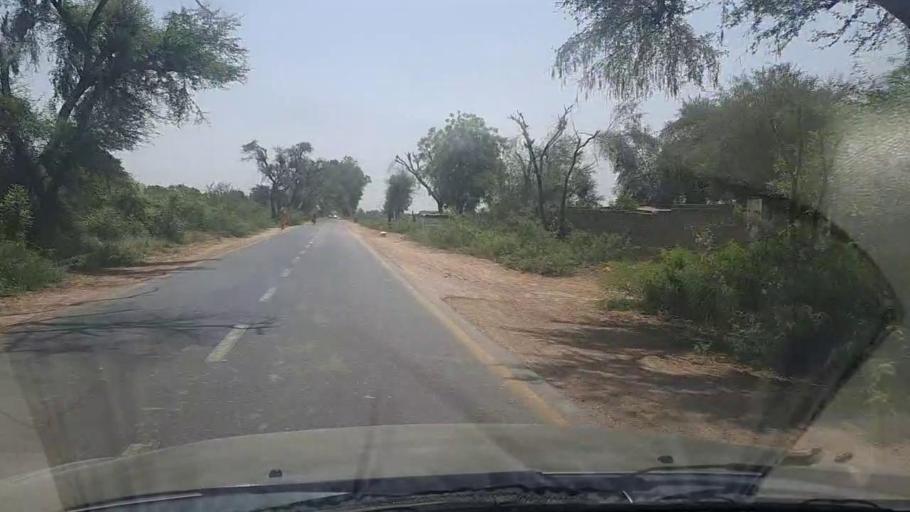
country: PK
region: Sindh
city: Tando Jam
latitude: 25.3240
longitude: 68.5502
